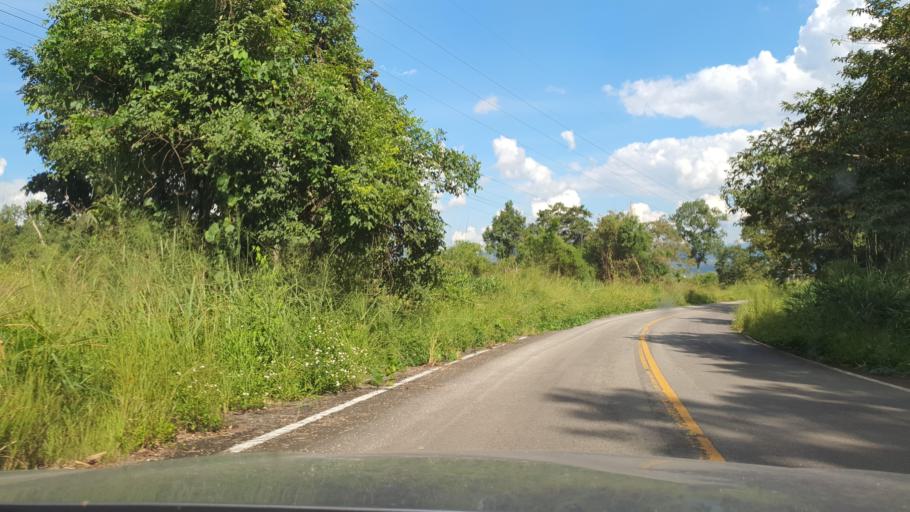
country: TH
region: Chiang Rai
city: Wiang Pa Pao
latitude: 19.3310
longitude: 99.4635
